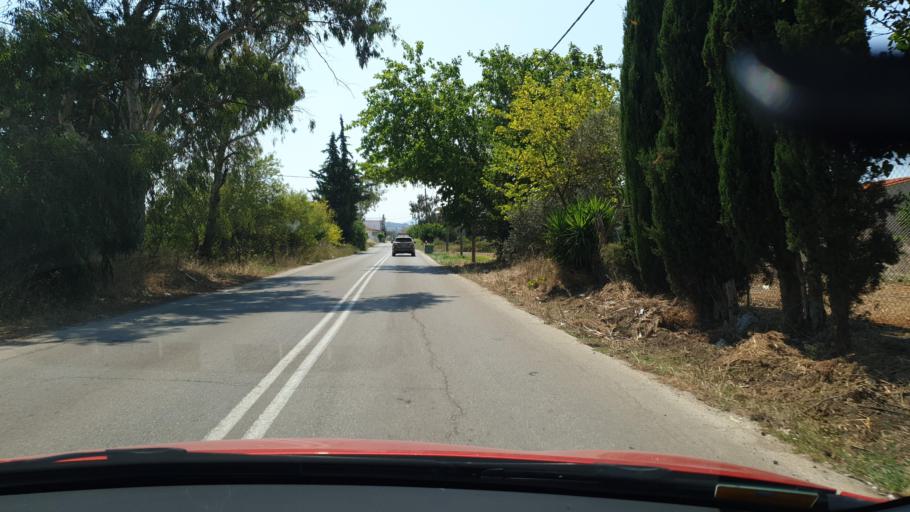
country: GR
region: Central Greece
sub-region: Nomos Evvoias
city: Aliveri
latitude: 38.4716
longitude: 24.1168
